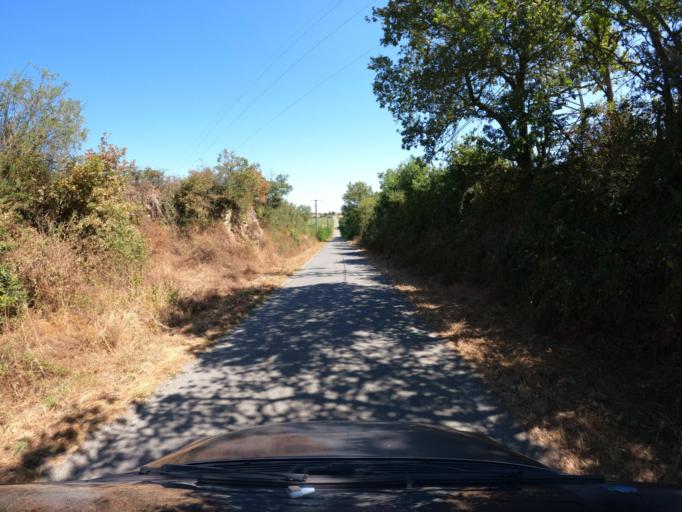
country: FR
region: Pays de la Loire
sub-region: Departement de Maine-et-Loire
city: Saint-Christophe-du-Bois
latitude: 47.0390
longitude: -0.9531
